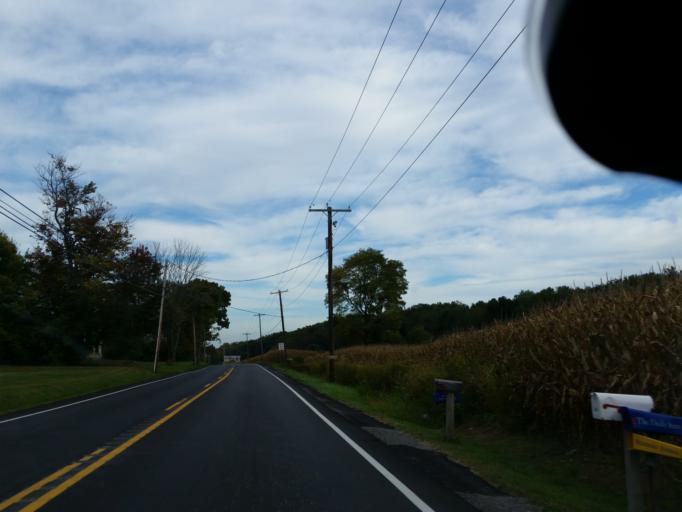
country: US
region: Pennsylvania
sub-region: Northumberland County
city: Dewart
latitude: 41.1108
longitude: -76.9103
